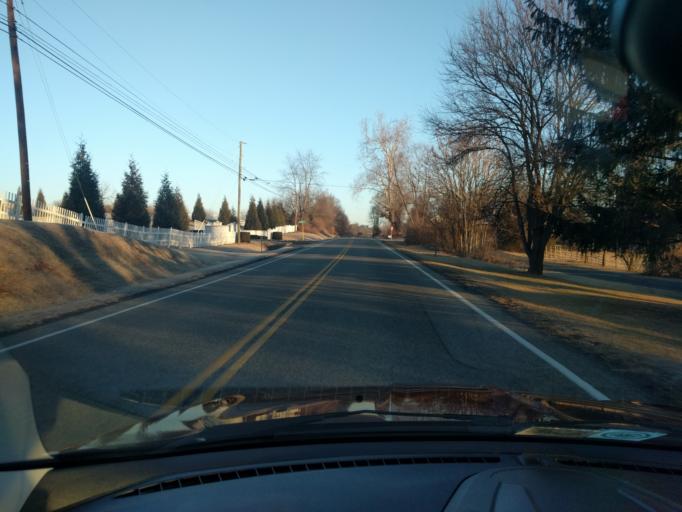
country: US
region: Virginia
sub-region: Augusta County
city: Weyers Cave
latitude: 38.3022
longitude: -78.9345
